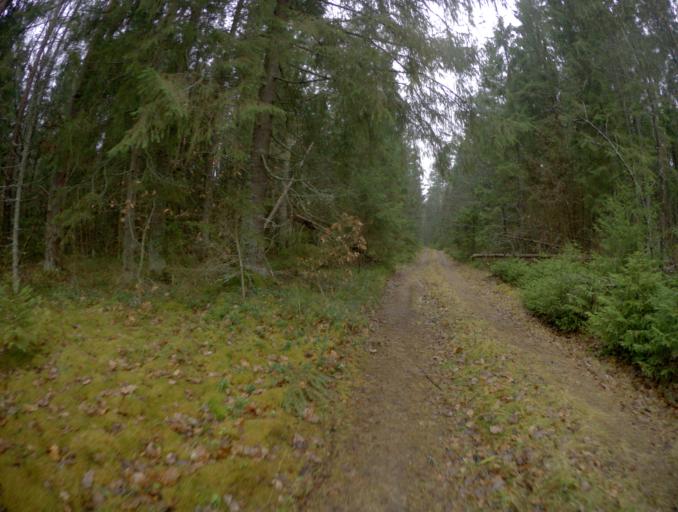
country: RU
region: Vladimir
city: Golovino
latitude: 56.0082
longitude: 40.4826
